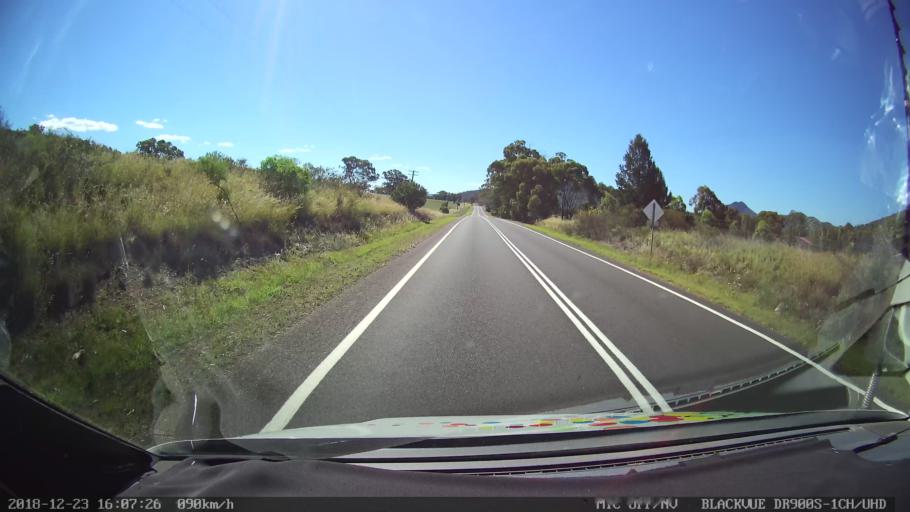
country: AU
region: New South Wales
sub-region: Tamworth Municipality
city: Phillip
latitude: -31.2714
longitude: 150.7623
